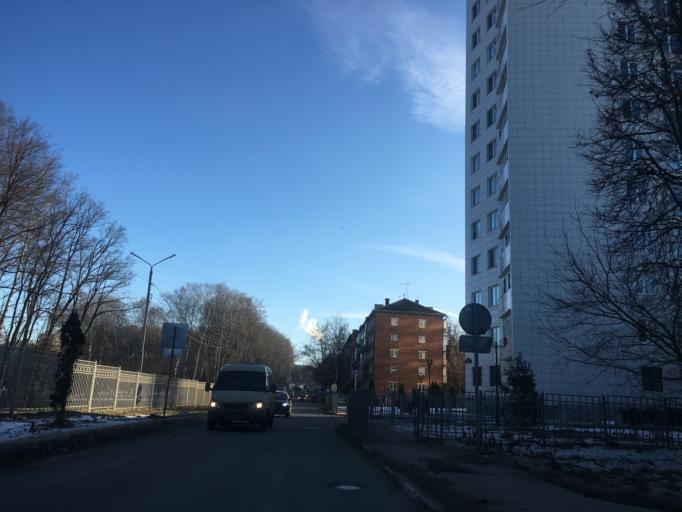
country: RU
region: Tula
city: Mendeleyevskiy
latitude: 54.1761
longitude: 37.5815
